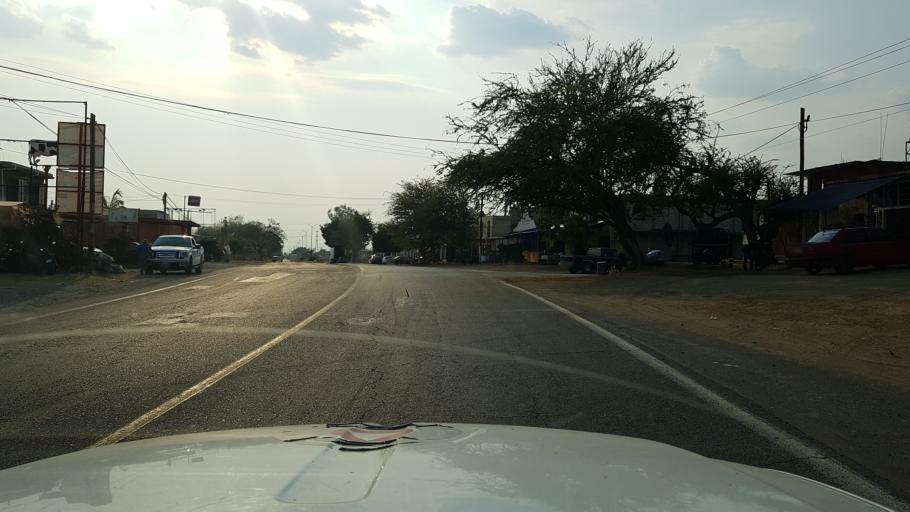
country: MX
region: Morelos
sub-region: Yecapixtla
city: Yecapixtla
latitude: 18.8892
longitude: -98.8768
